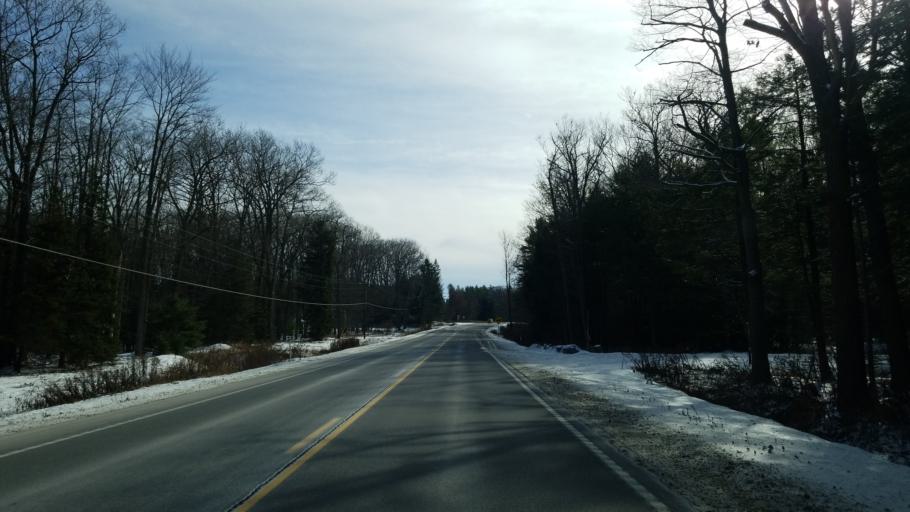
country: US
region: Pennsylvania
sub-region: Clearfield County
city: Clearfield
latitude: 41.1267
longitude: -78.5353
